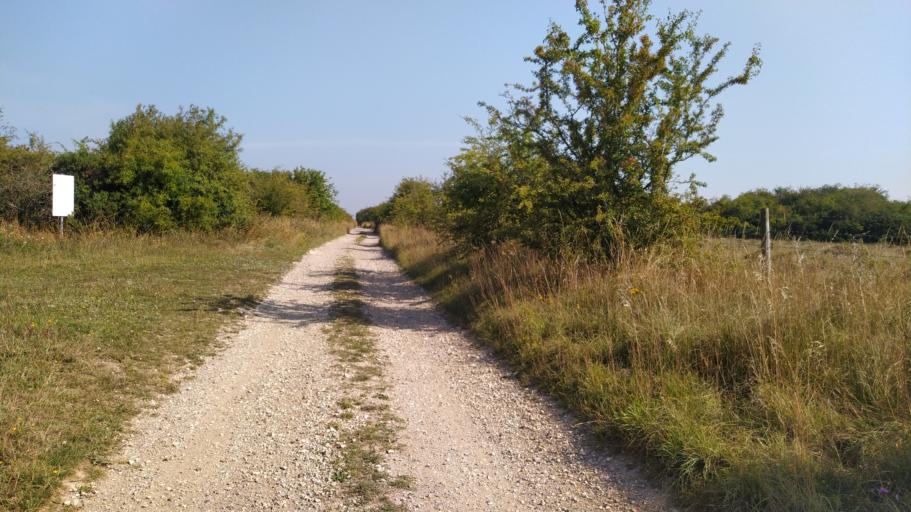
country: GB
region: England
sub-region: Wiltshire
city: Winterbourne Stoke
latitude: 51.1696
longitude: -1.9522
